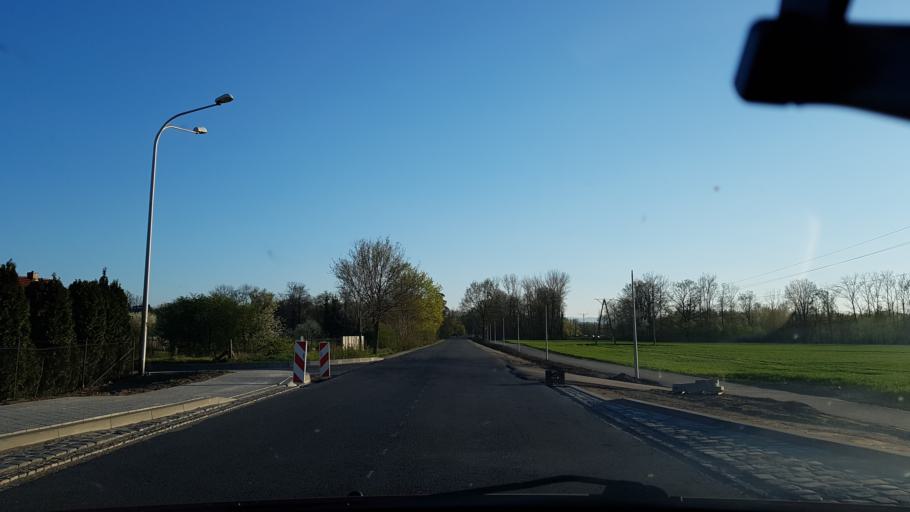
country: PL
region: Opole Voivodeship
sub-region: Powiat nyski
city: Nysa
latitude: 50.4379
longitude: 17.3040
